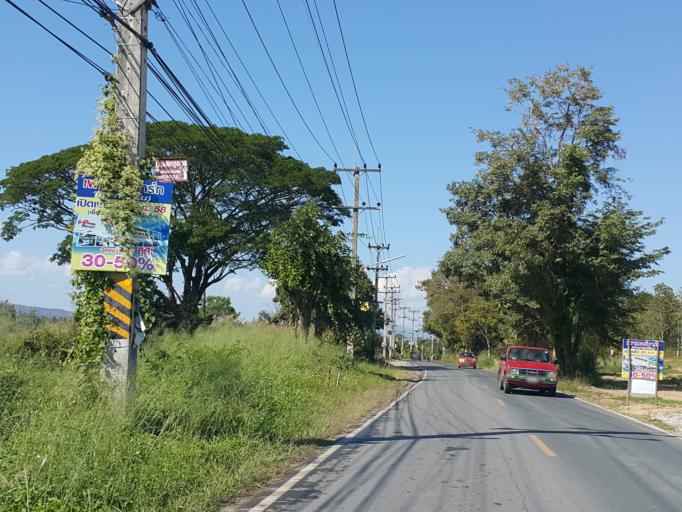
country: TH
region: Chiang Mai
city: San Sai
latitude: 18.9435
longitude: 98.9285
